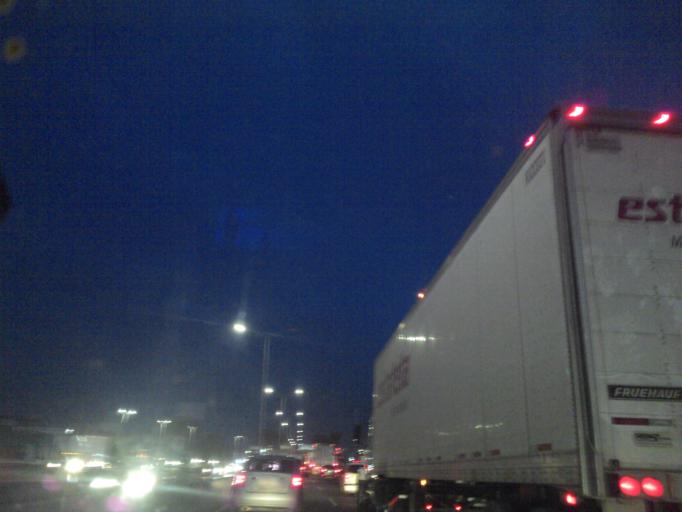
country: MX
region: Jalisco
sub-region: San Pedro Tlaquepaque
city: Paseo del Prado
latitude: 20.6037
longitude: -103.3982
